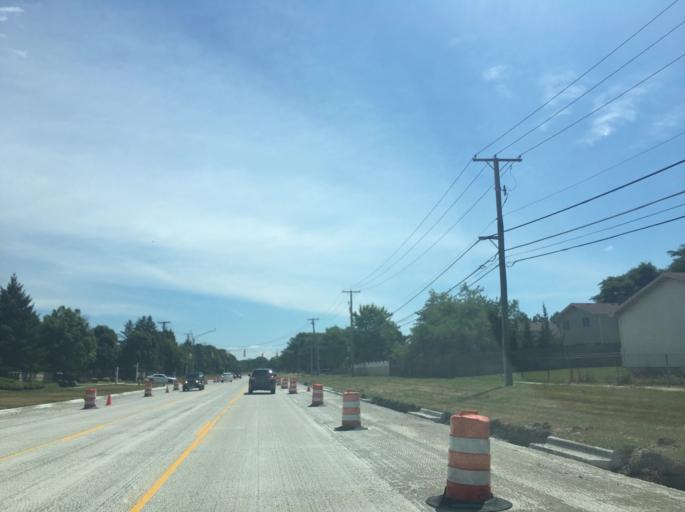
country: US
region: Michigan
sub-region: Macomb County
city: Clinton
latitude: 42.6132
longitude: -82.9429
